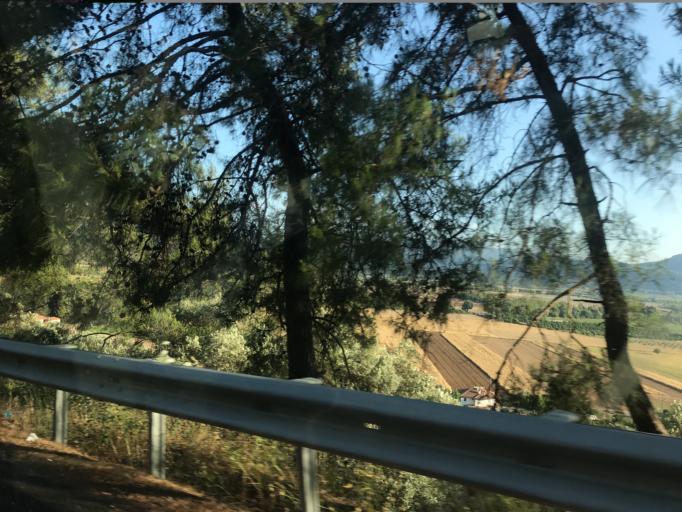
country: TR
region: Mugla
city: Ula
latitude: 37.0561
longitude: 28.3494
